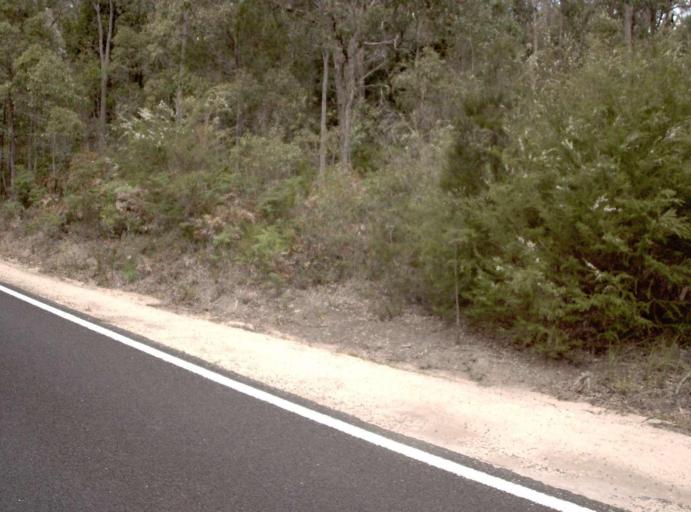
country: AU
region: New South Wales
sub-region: Bega Valley
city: Eden
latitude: -37.4056
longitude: 149.6638
